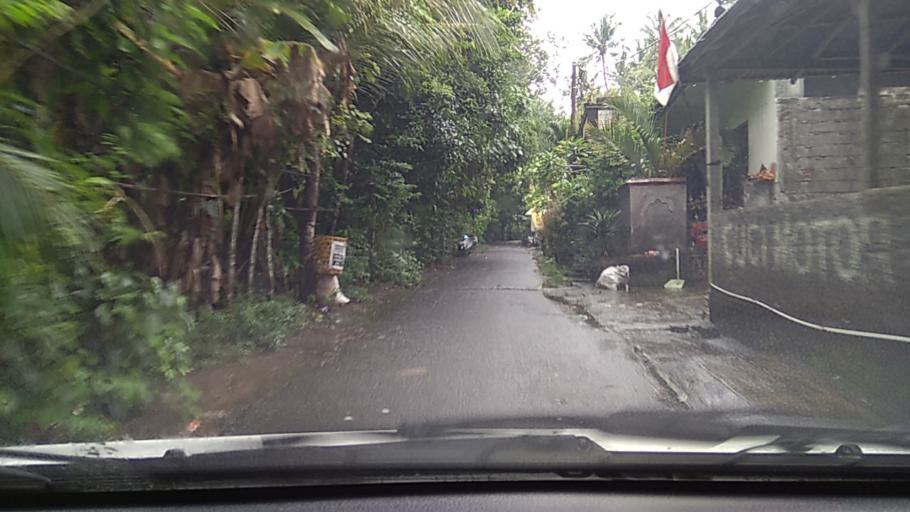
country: ID
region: Bali
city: Banjar Bugbug
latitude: -8.5122
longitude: 115.5791
